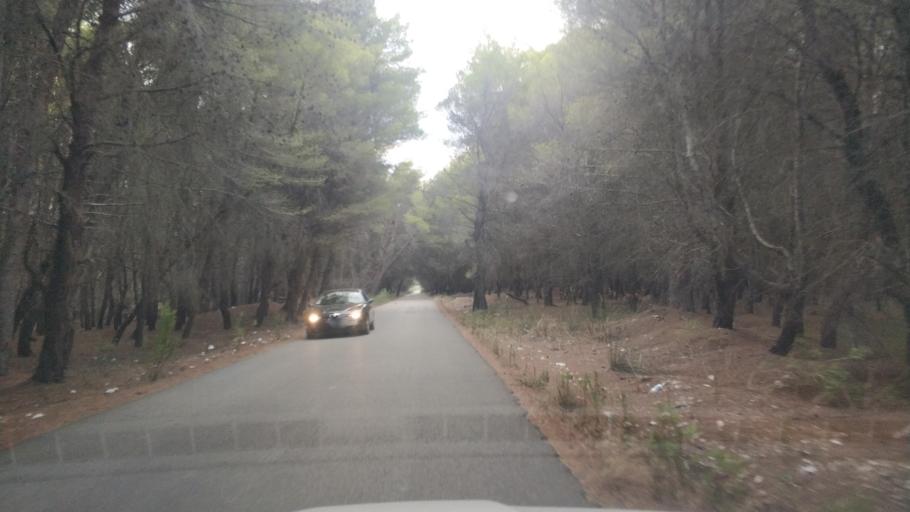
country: AL
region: Vlore
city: Vlore
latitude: 40.4975
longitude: 19.4316
